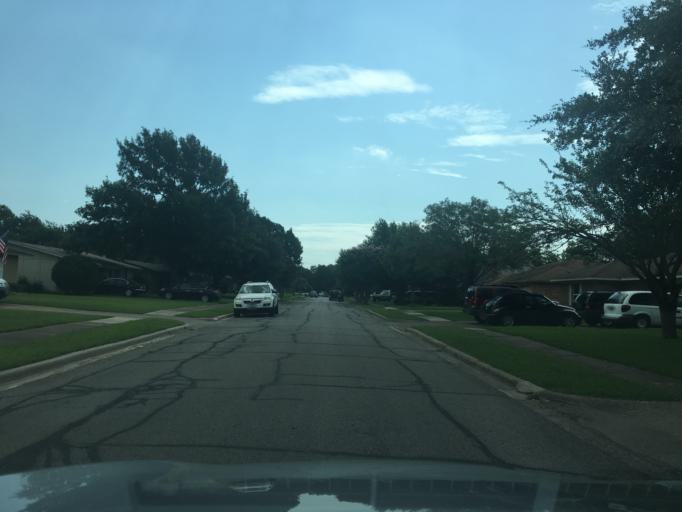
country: US
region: Texas
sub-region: Dallas County
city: Farmers Branch
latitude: 32.9280
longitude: -96.8674
